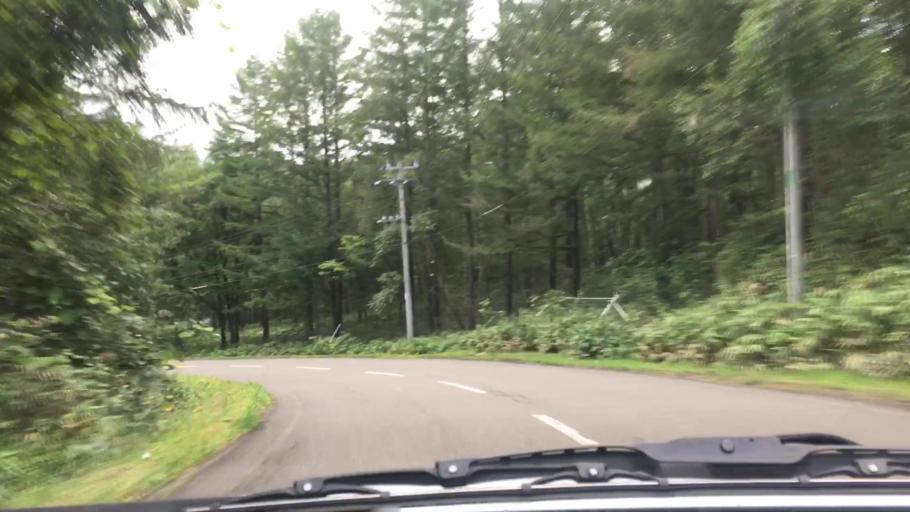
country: JP
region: Hokkaido
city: Otofuke
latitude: 43.1552
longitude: 142.8577
